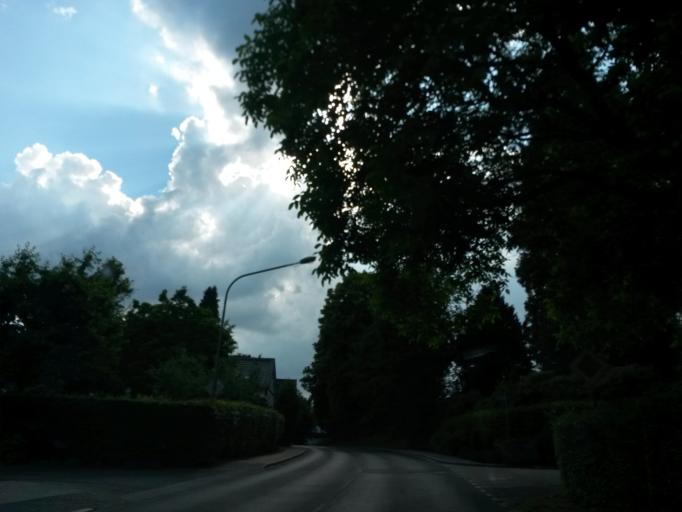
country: DE
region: North Rhine-Westphalia
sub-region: Regierungsbezirk Koln
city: Overath
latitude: 50.8737
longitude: 7.3160
